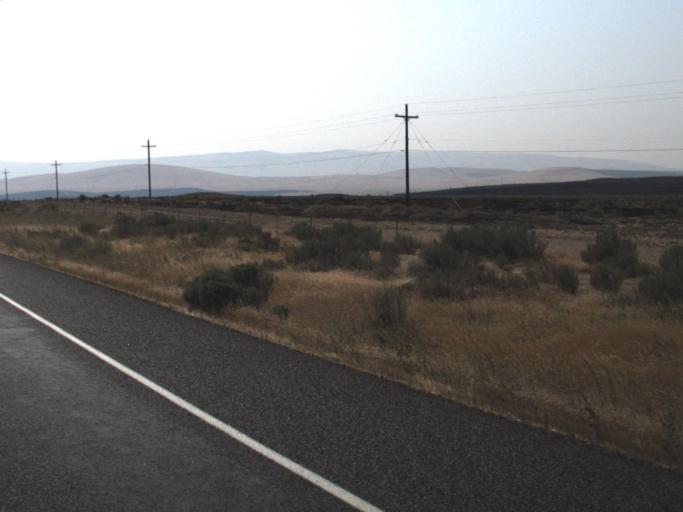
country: US
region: Washington
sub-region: Grant County
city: Desert Aire
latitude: 46.5970
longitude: -119.7274
